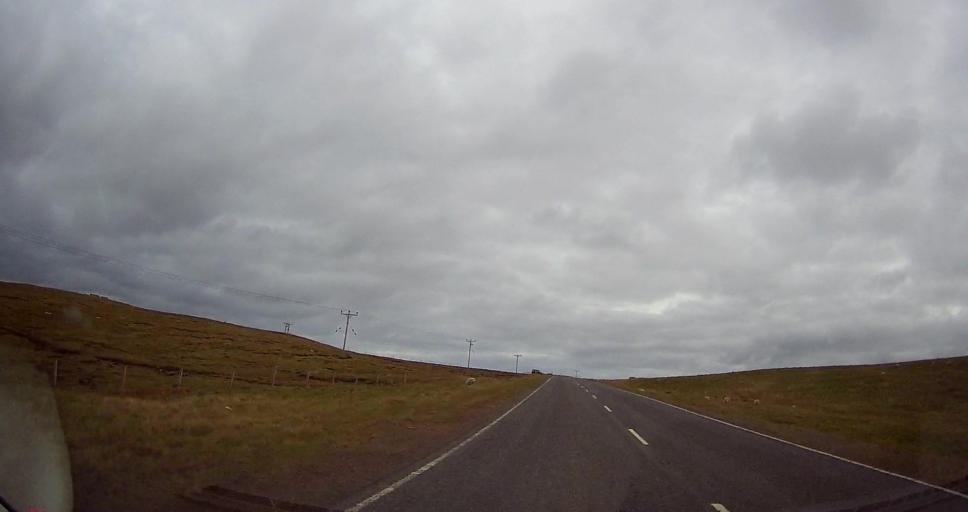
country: GB
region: Scotland
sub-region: Shetland Islands
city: Shetland
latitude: 60.6545
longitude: -1.0681
